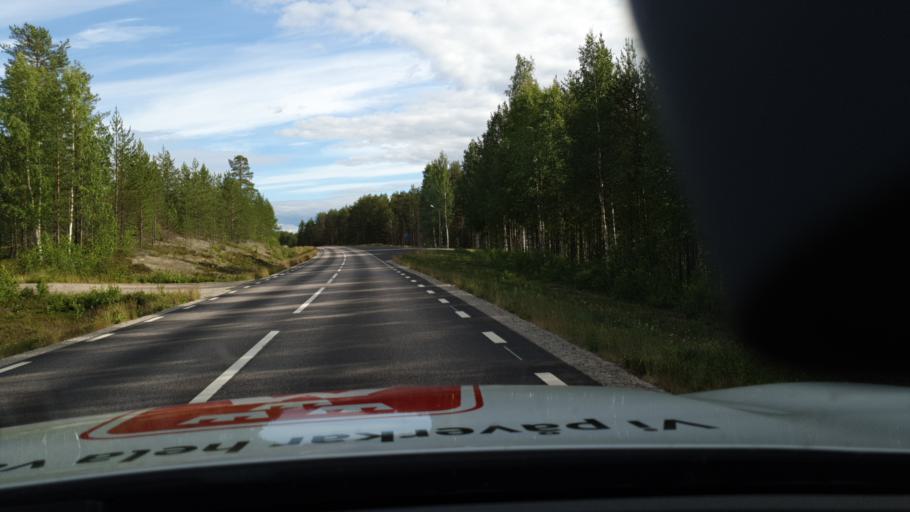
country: SE
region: Norrbotten
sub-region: Overkalix Kommun
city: OEverkalix
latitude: 66.4446
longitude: 22.7862
